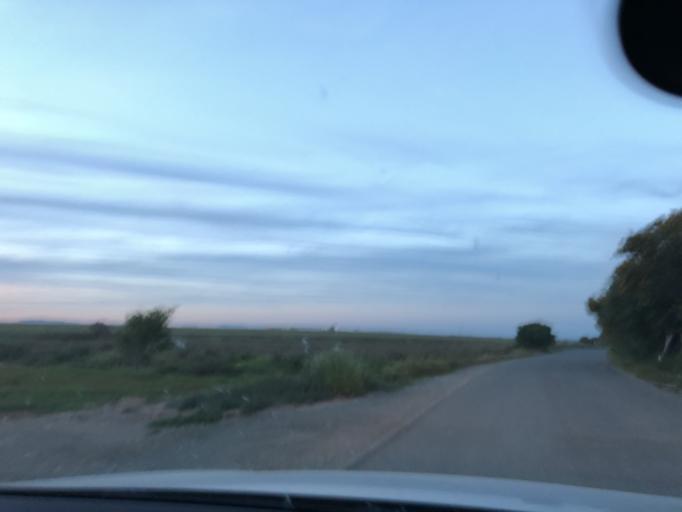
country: CY
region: Larnaka
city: Meneou
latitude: 34.8594
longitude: 33.6311
